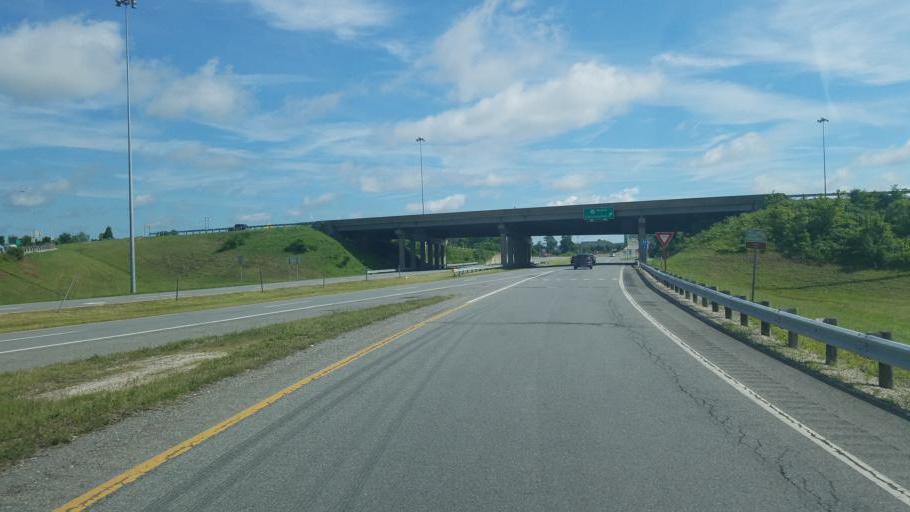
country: US
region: West Virginia
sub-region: Mason County
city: Point Pleasant
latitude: 38.8301
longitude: -82.1429
